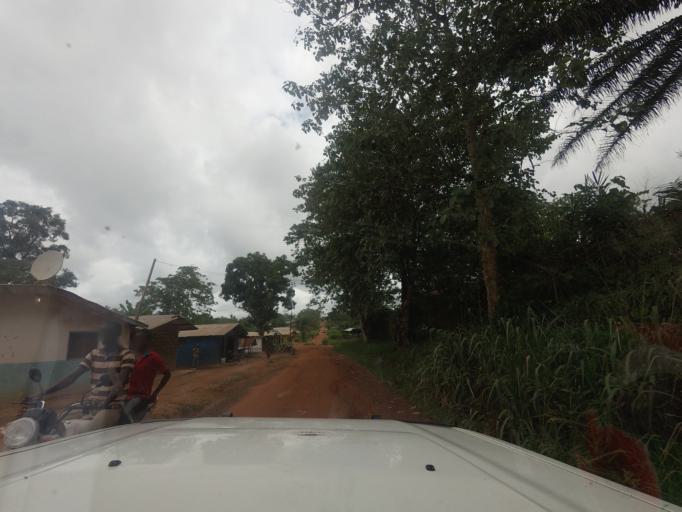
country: LR
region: Grand Gedeh
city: Zwedru
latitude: 6.0671
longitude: -8.1378
